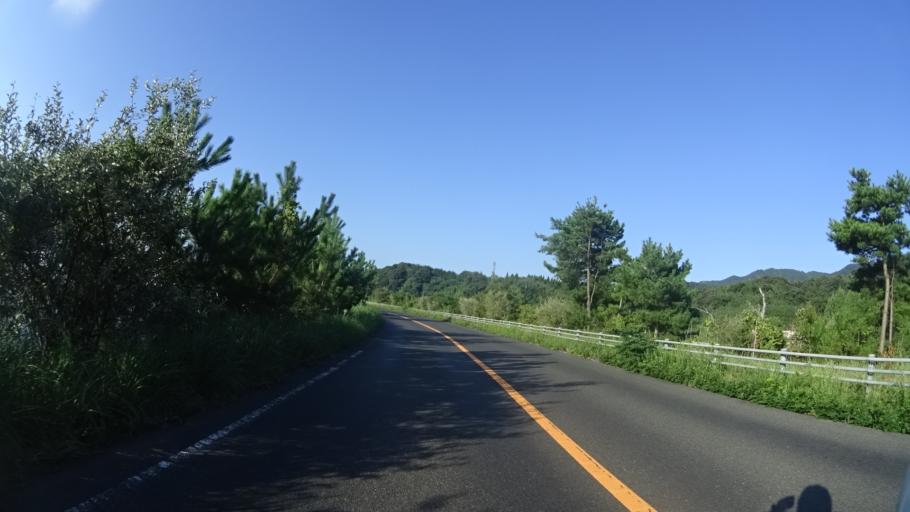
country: JP
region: Shimane
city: Sakaiminato
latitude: 35.5361
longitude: 133.1546
